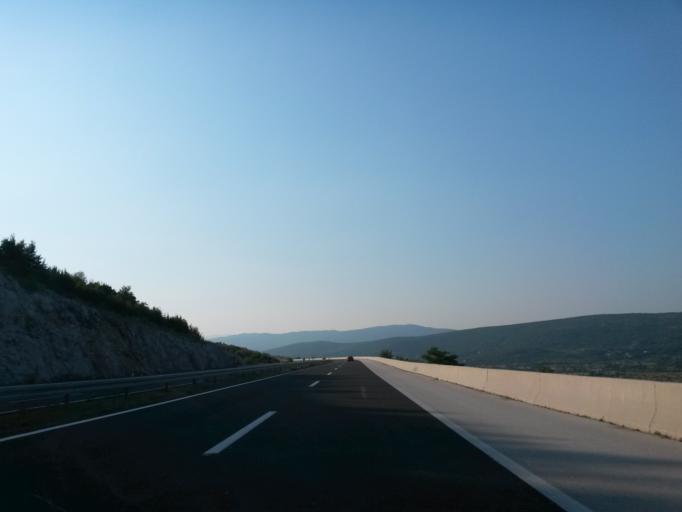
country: HR
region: Splitsko-Dalmatinska
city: Dugopolje
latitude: 43.5963
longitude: 16.6255
